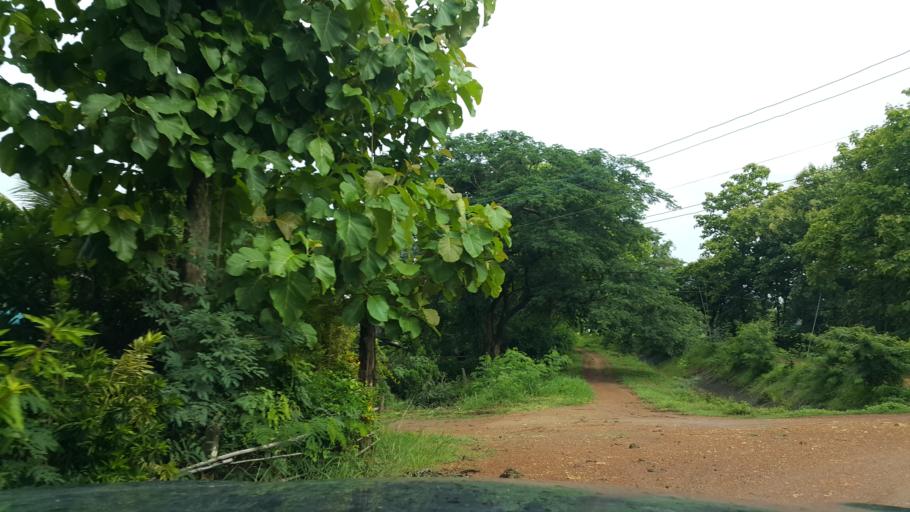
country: TH
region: Chiang Mai
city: San Kamphaeng
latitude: 18.7351
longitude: 99.1656
